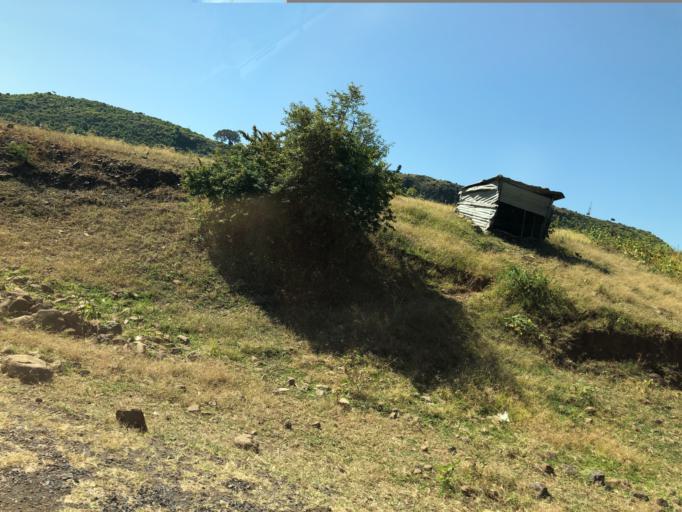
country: ET
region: Amhara
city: Adis Zemen
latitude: 12.1843
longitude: 37.6759
